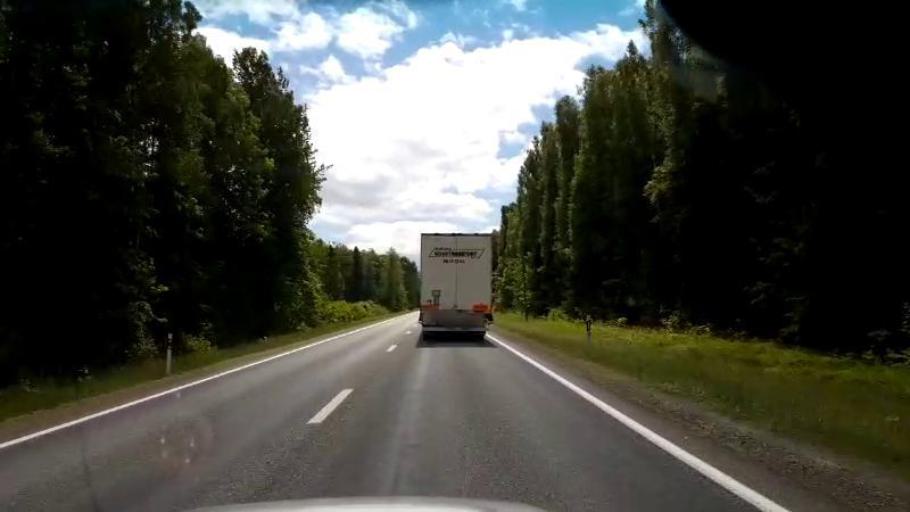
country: LV
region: Salacgrivas
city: Salacgriva
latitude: 57.5928
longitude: 24.4169
